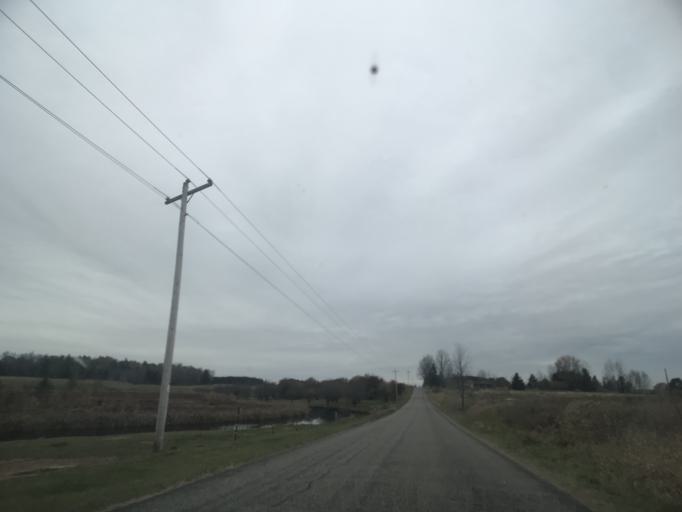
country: US
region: Wisconsin
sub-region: Menominee County
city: Legend Lake
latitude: 45.1813
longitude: -88.4570
